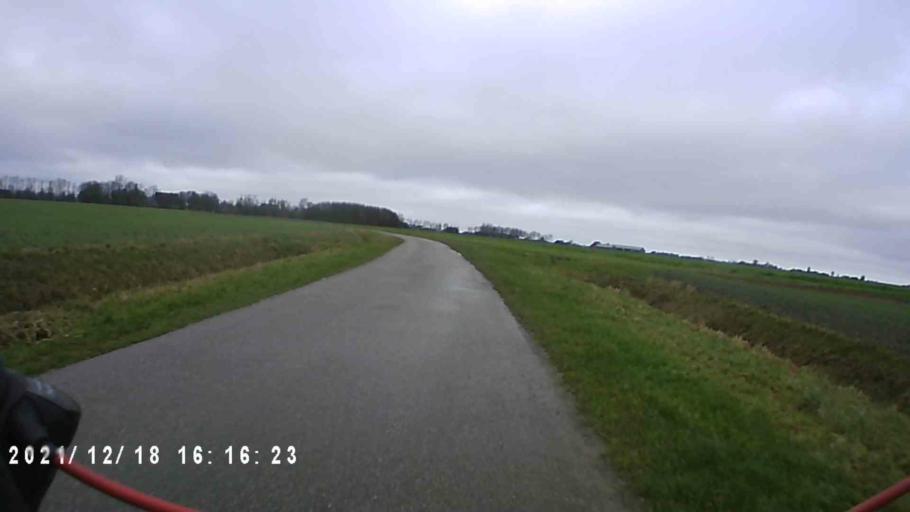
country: NL
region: Friesland
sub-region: Gemeente Dongeradeel
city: Anjum
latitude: 53.3723
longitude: 6.0600
